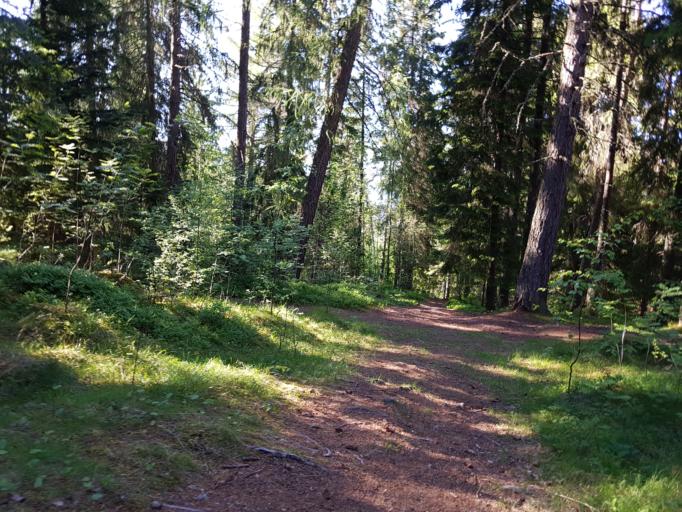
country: NO
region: Sor-Trondelag
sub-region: Trondheim
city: Trondheim
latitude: 63.4226
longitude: 10.3626
